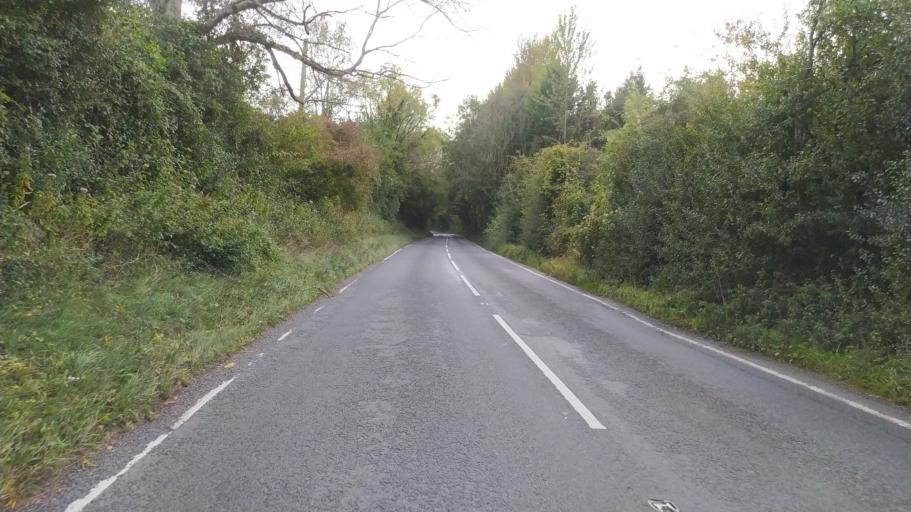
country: GB
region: England
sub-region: Hampshire
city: Romsey
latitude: 51.0524
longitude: -1.5164
